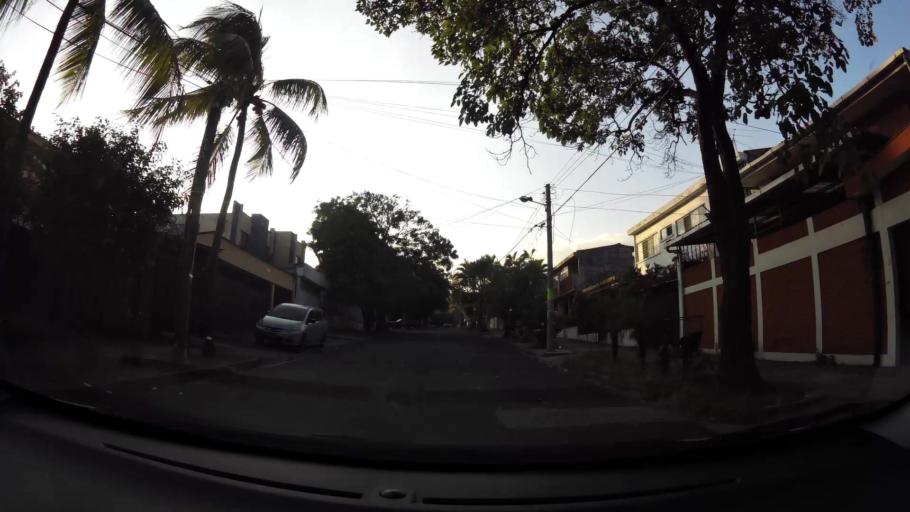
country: SV
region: San Salvador
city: Cuscatancingo
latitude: 13.7152
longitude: -89.1998
